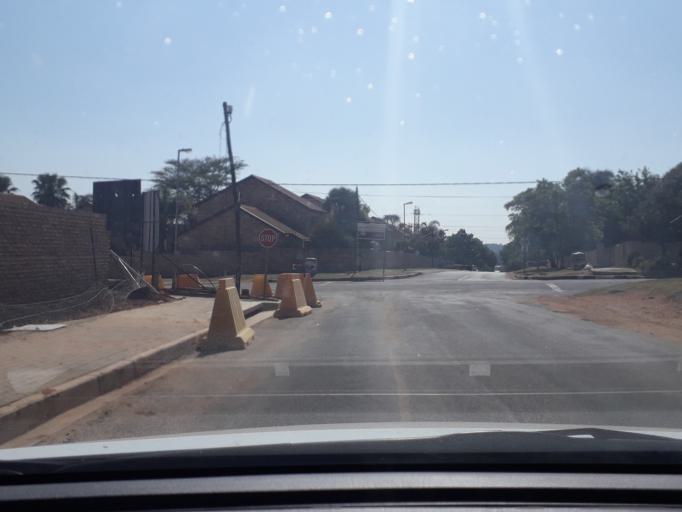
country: ZA
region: Gauteng
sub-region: City of Johannesburg Metropolitan Municipality
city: Roodepoort
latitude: -26.0820
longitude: 27.9630
